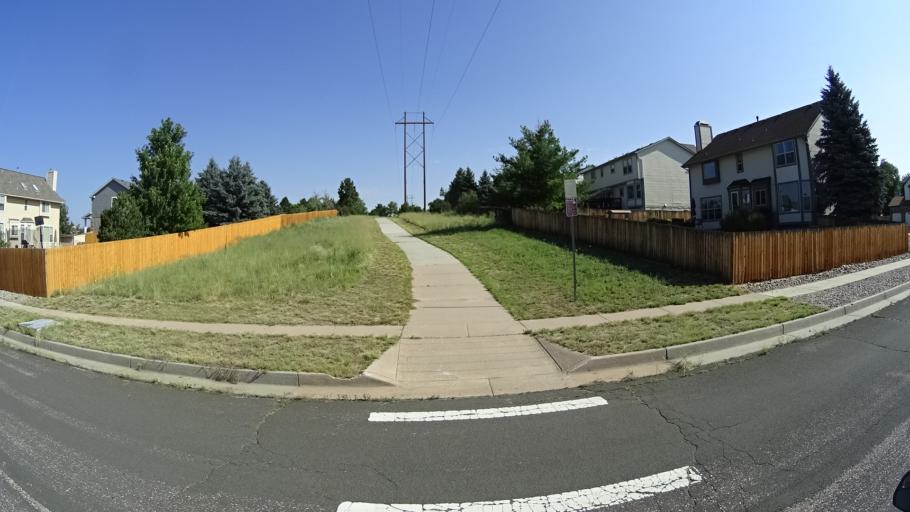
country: US
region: Colorado
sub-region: El Paso County
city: Air Force Academy
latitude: 38.9527
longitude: -104.7843
